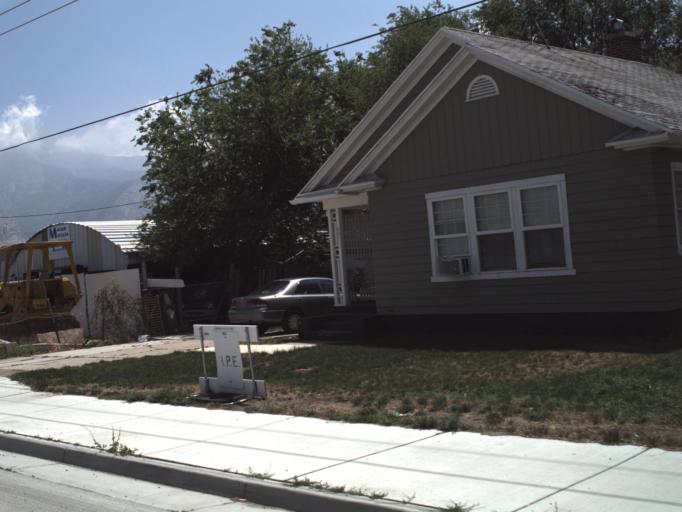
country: US
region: Utah
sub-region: Weber County
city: Marriott-Slaterville
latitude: 41.2444
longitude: -111.9970
